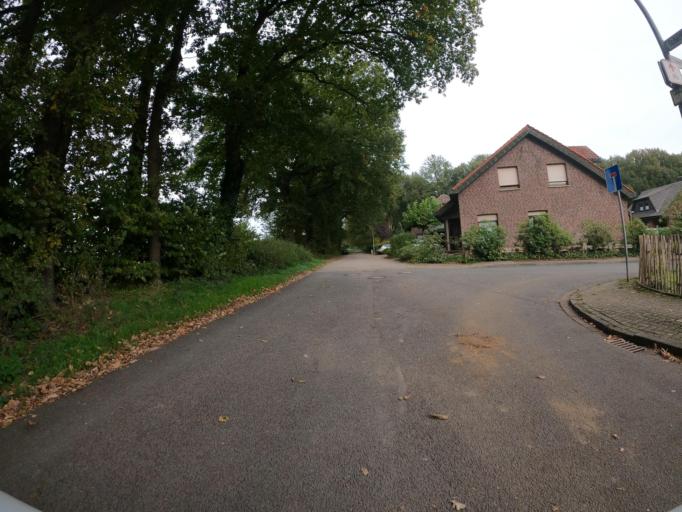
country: DE
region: North Rhine-Westphalia
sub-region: Regierungsbezirk Dusseldorf
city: Schermbeck
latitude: 51.7016
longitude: 6.8849
